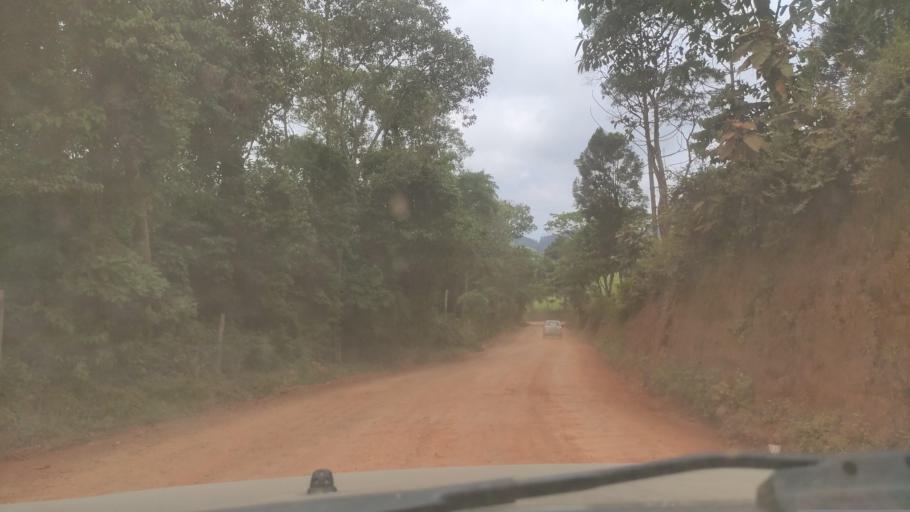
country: BR
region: Minas Gerais
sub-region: Cambui
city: Cambui
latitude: -22.6594
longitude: -45.9031
